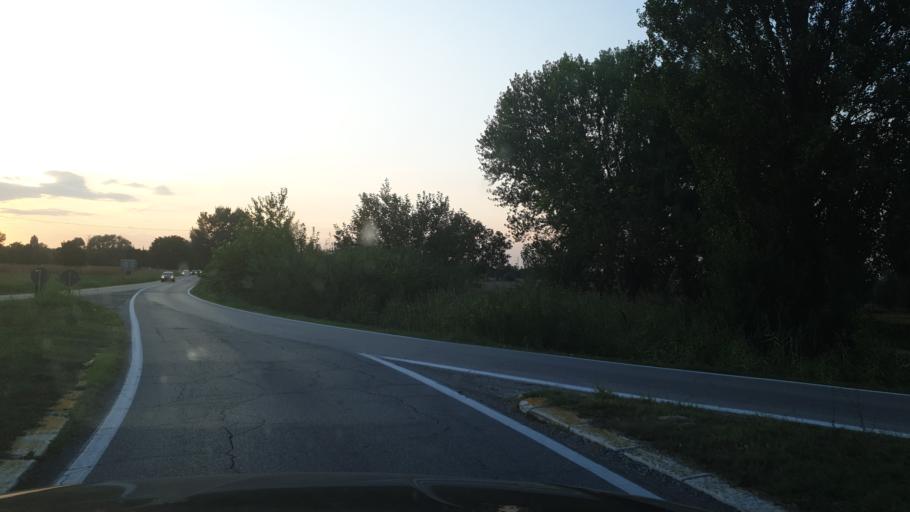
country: IT
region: Emilia-Romagna
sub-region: Provincia di Bologna
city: Progresso
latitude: 44.5654
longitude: 11.4000
